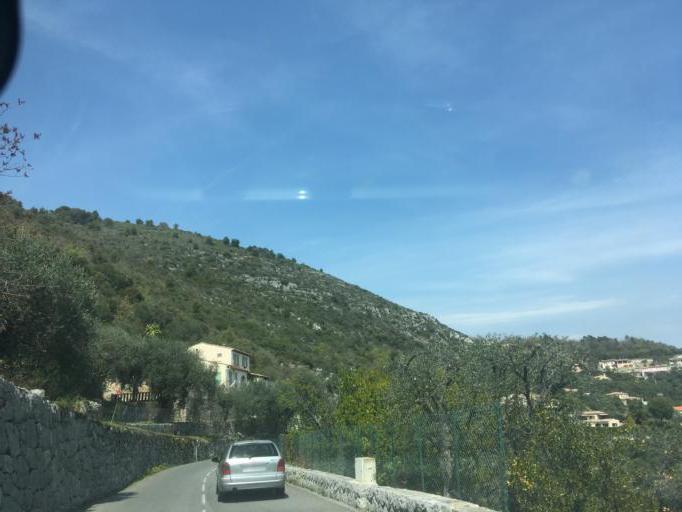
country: FR
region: Provence-Alpes-Cote d'Azur
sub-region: Departement des Alpes-Maritimes
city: Levens
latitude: 43.8421
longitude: 7.2149
